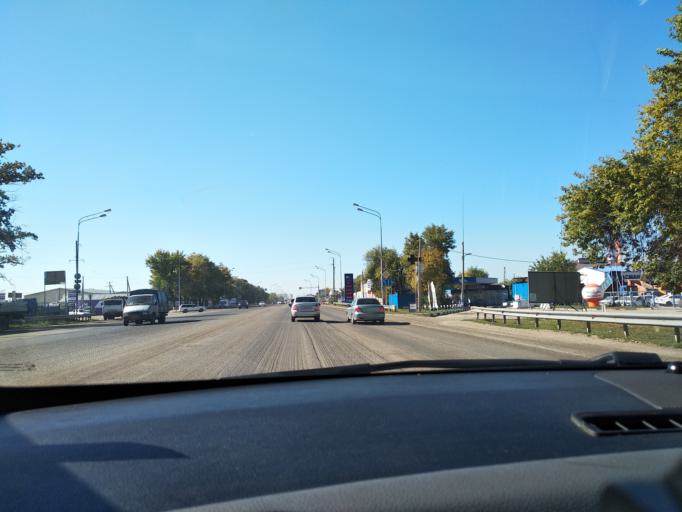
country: RU
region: Krasnodarskiy
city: Krasnodar
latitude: 45.1340
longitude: 39.0257
